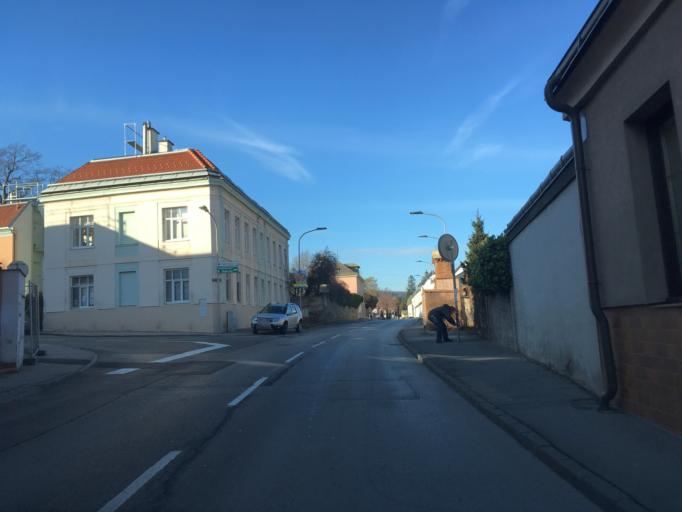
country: AT
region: Lower Austria
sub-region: Politischer Bezirk Wien-Umgebung
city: Klosterneuburg
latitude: 48.3173
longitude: 16.3127
